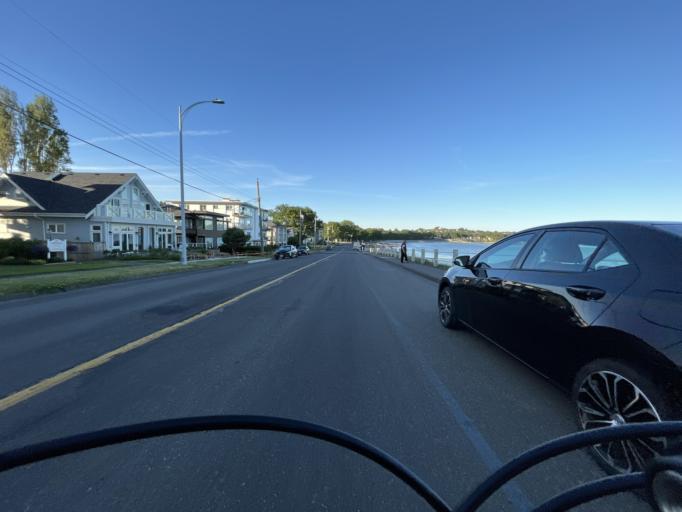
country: CA
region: British Columbia
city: Victoria
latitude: 48.4076
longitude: -123.3471
